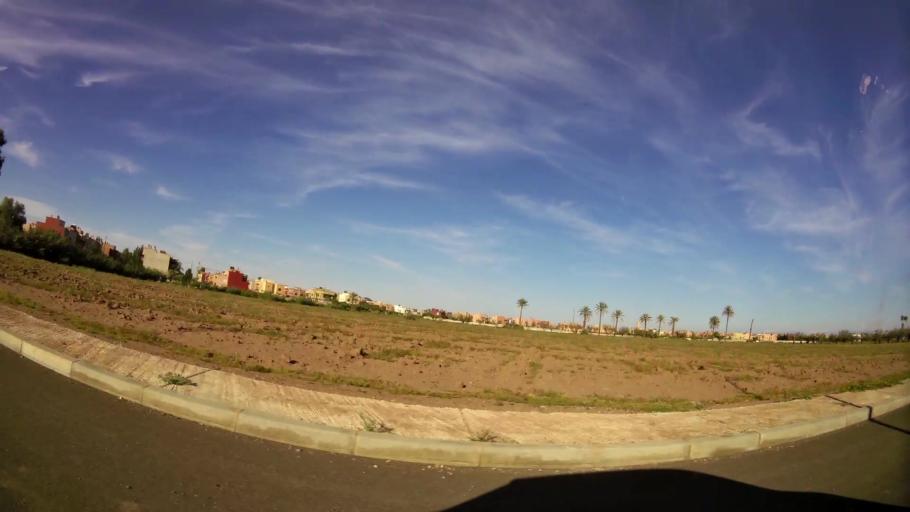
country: MA
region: Marrakech-Tensift-Al Haouz
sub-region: Marrakech
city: Marrakesh
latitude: 31.6740
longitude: -8.0647
